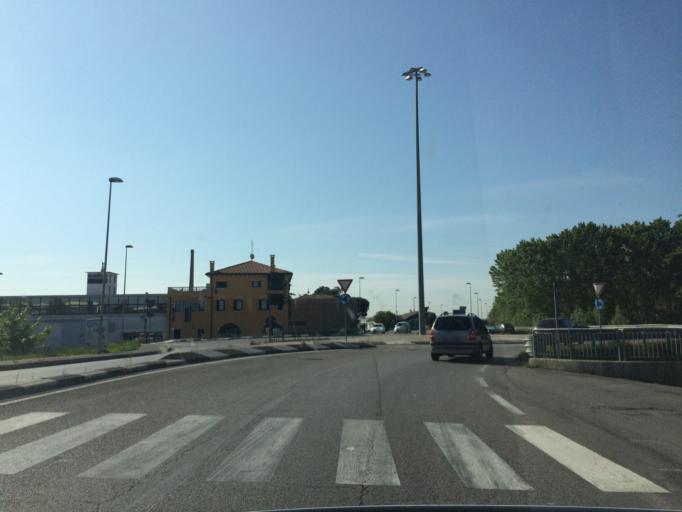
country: IT
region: Veneto
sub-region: Provincia di Padova
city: Pieve
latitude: 45.5309
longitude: 11.8301
